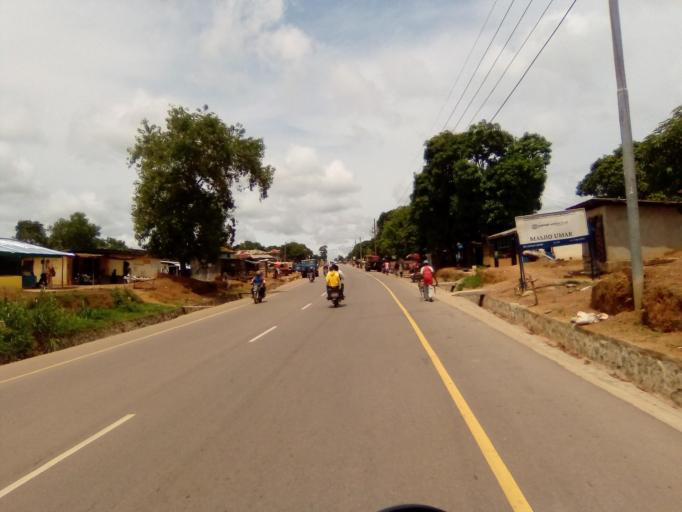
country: SL
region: Southern Province
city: Bo
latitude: 7.9353
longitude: -11.7257
